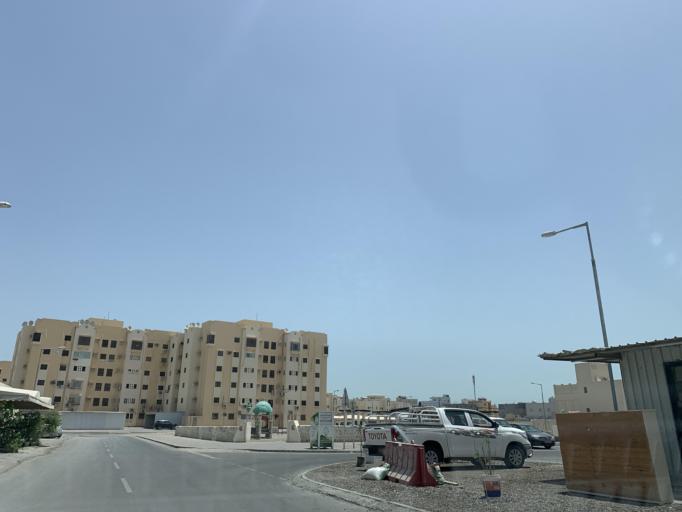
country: BH
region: Northern
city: Sitrah
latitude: 26.1415
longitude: 50.5942
